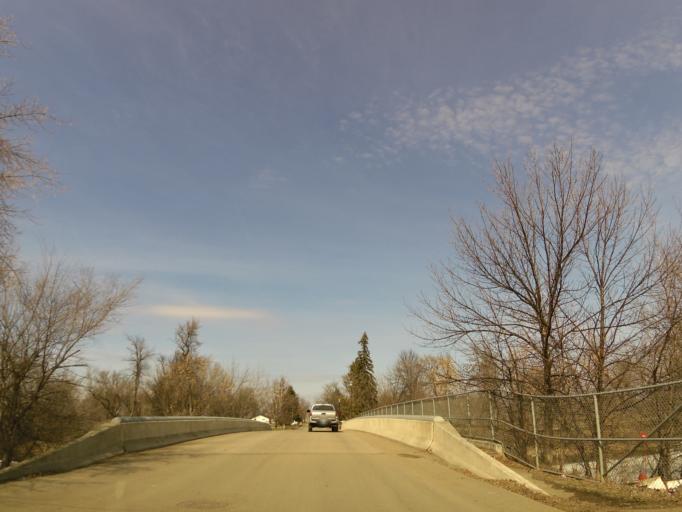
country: US
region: North Dakota
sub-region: Walsh County
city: Grafton
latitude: 48.4229
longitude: -97.4085
